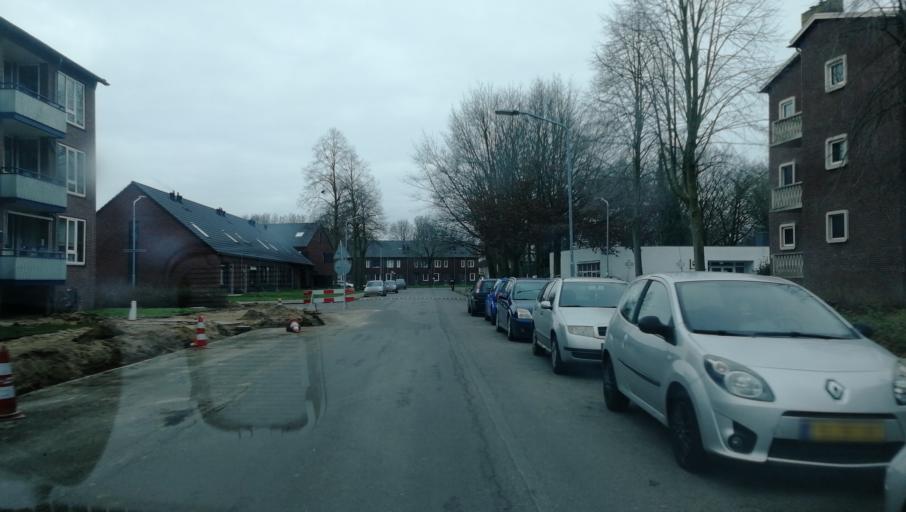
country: NL
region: Limburg
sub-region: Gemeente Venlo
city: Tegelen
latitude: 51.3658
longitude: 6.1414
